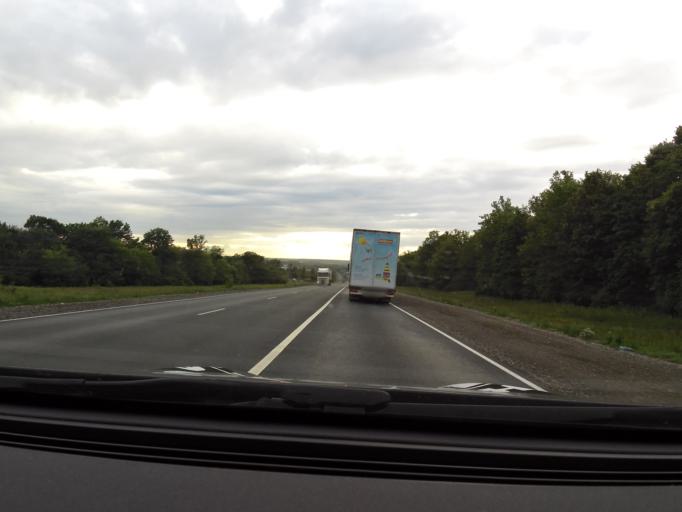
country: RU
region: Chuvashia
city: Tsivil'sk
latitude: 55.8432
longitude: 47.5277
